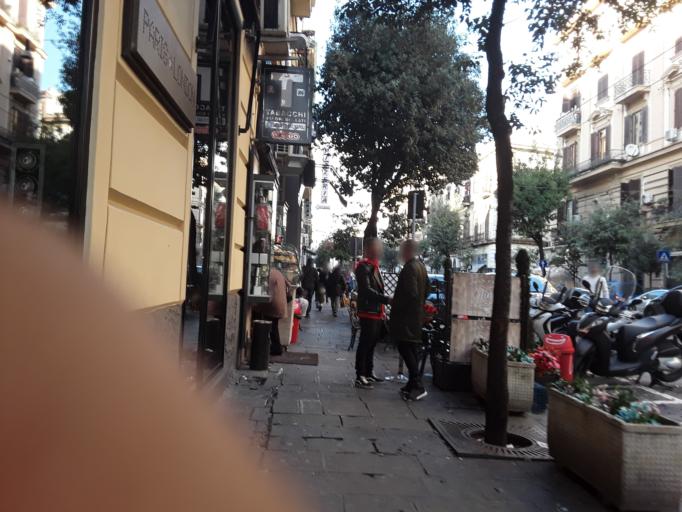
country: IT
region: Campania
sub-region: Provincia di Napoli
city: Napoli
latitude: 40.8585
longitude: 14.2670
